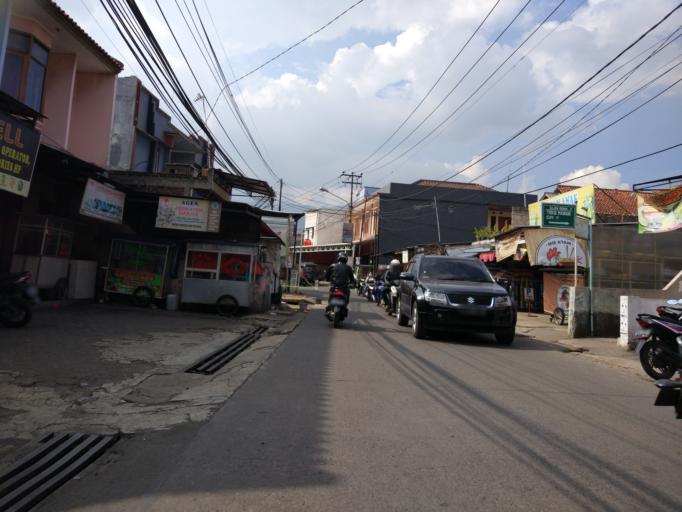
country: ID
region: West Java
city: Cileunyi
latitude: -6.9085
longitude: 107.6908
